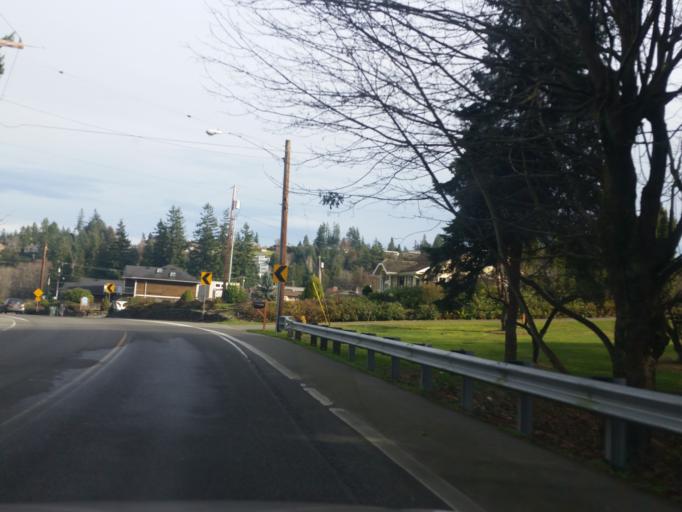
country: US
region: Washington
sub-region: Snohomish County
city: Mukilteo
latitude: 47.9573
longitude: -122.2557
